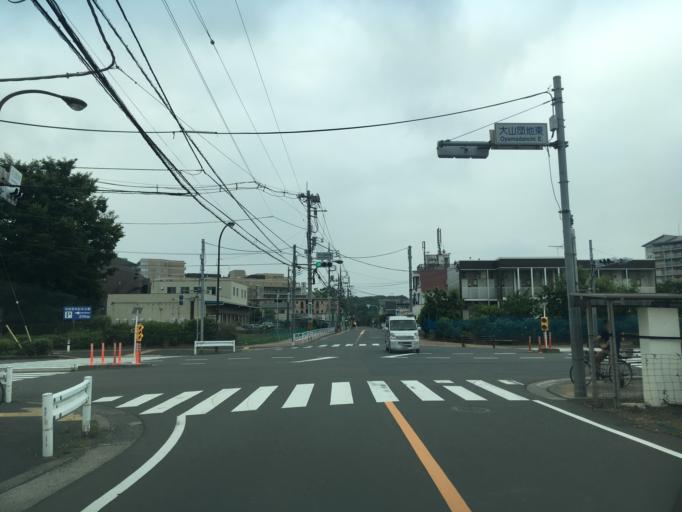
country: JP
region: Tokyo
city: Hino
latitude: 35.7210
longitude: 139.3967
